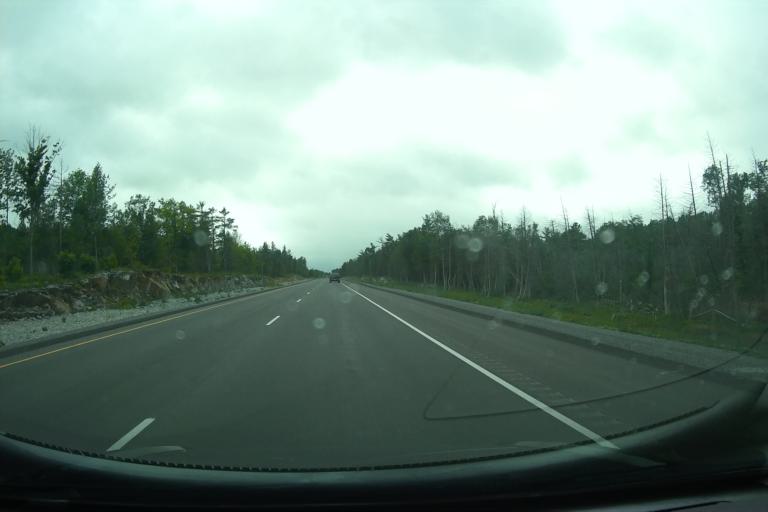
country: CA
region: Ontario
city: Arnprior
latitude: 45.4368
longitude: -76.4273
